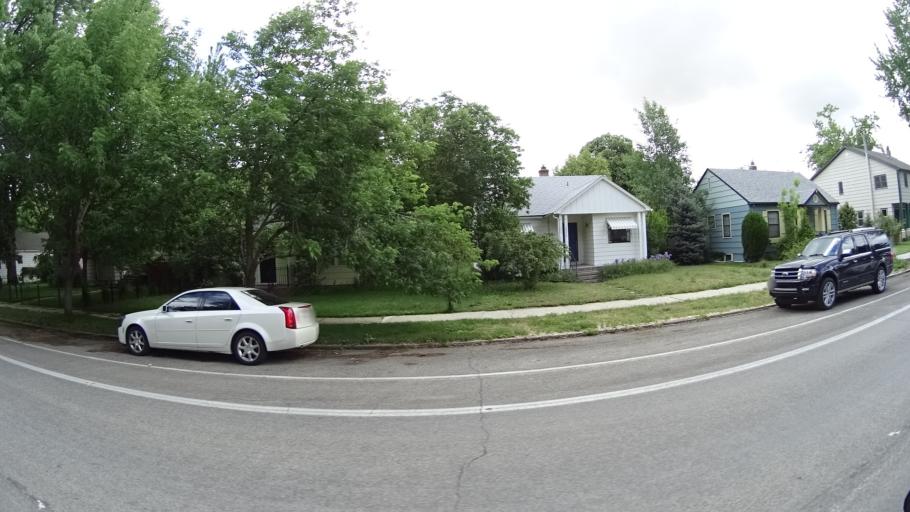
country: US
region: Idaho
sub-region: Ada County
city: Boise
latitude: 43.6370
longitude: -116.2058
